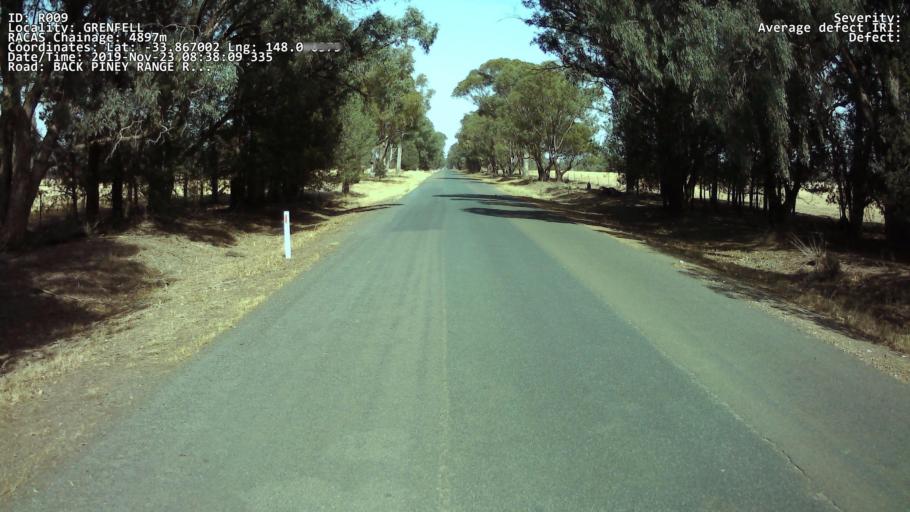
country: AU
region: New South Wales
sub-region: Weddin
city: Grenfell
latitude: -33.8670
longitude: 148.0604
